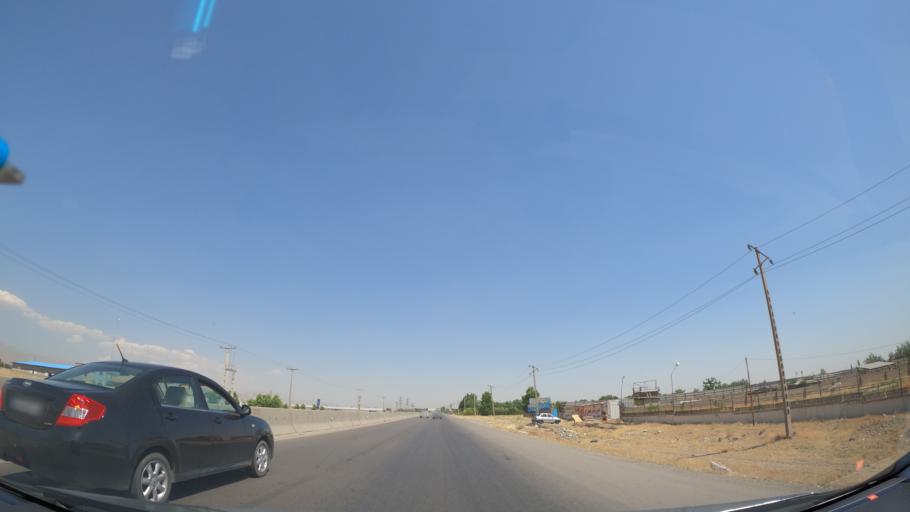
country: IR
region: Alborz
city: Hashtgerd
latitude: 35.9275
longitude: 50.7337
